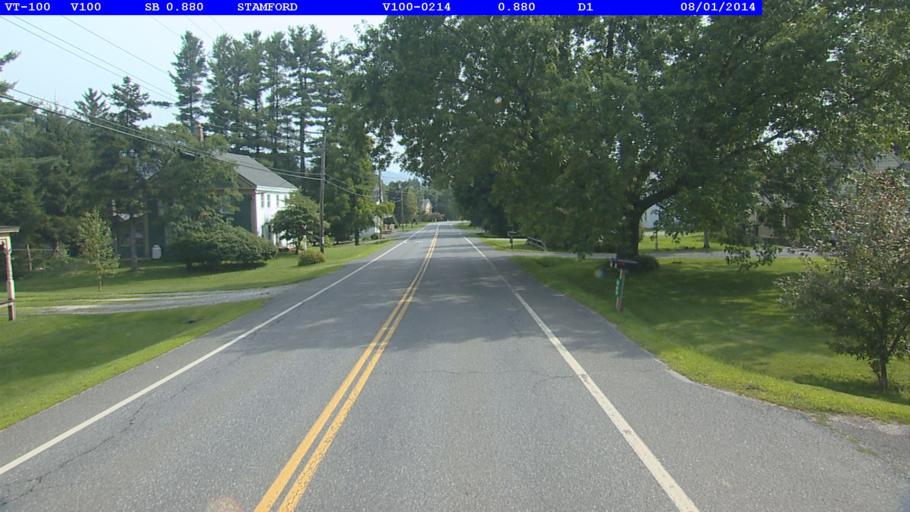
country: US
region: Massachusetts
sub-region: Berkshire County
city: North Adams
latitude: 42.7533
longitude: -73.0685
